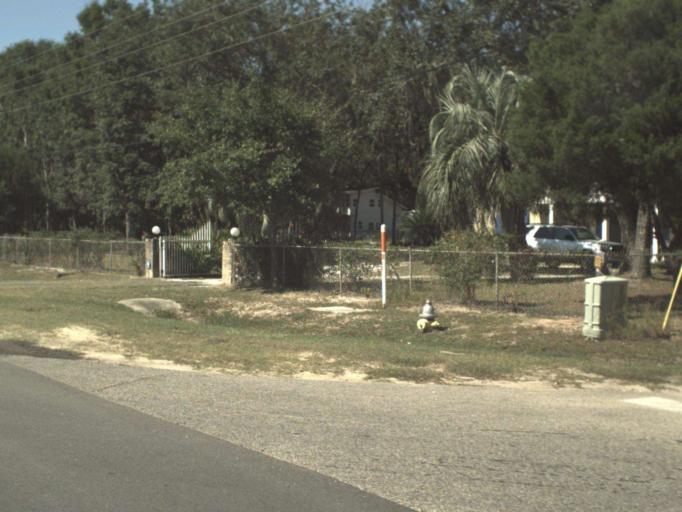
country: US
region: Florida
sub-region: Walton County
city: Miramar Beach
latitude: 30.4655
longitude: -86.3608
